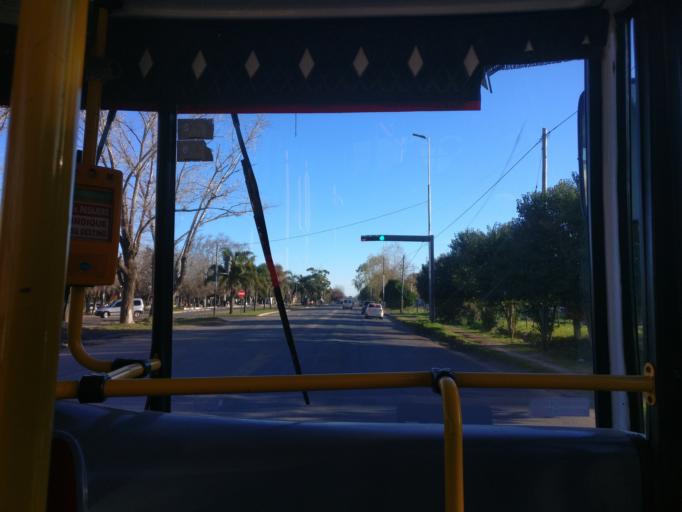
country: AR
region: Buenos Aires
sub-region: Partido de Ezeiza
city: Ezeiza
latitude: -34.9091
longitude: -58.5926
